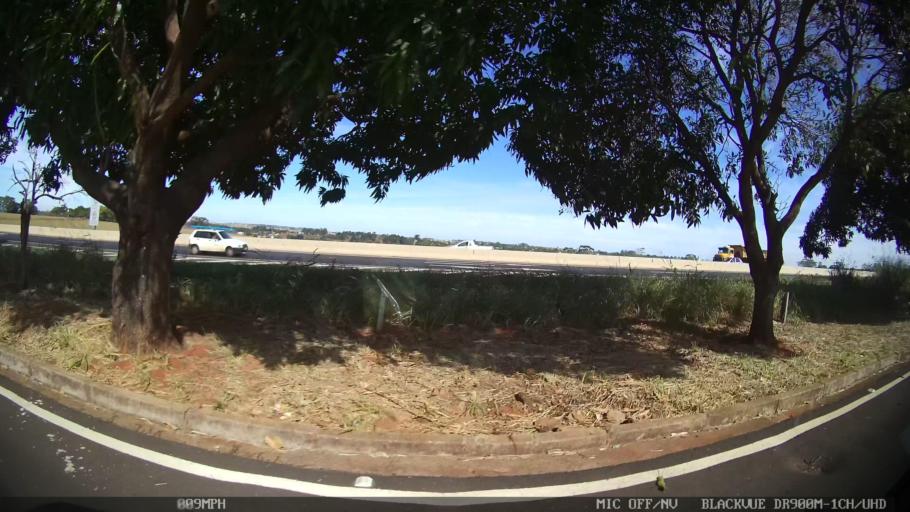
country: BR
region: Sao Paulo
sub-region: Sao Jose Do Rio Preto
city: Sao Jose do Rio Preto
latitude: -20.8503
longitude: -49.3866
